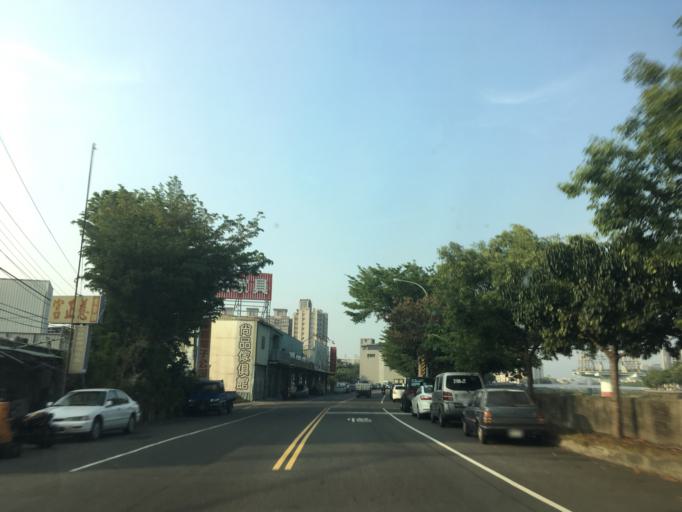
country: TW
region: Taiwan
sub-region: Taichung City
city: Taichung
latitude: 24.1490
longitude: 120.6995
